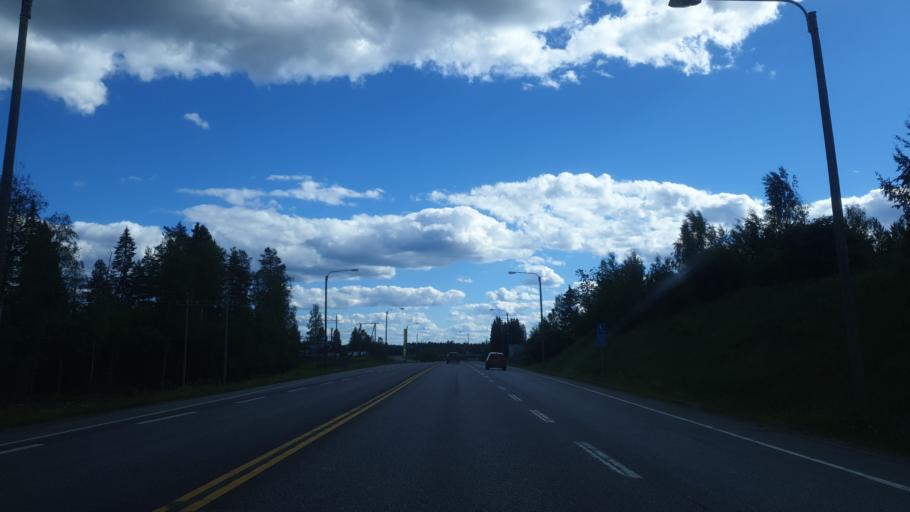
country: FI
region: Southern Savonia
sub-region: Pieksaemaeki
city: Juva
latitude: 61.9039
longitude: 27.8044
